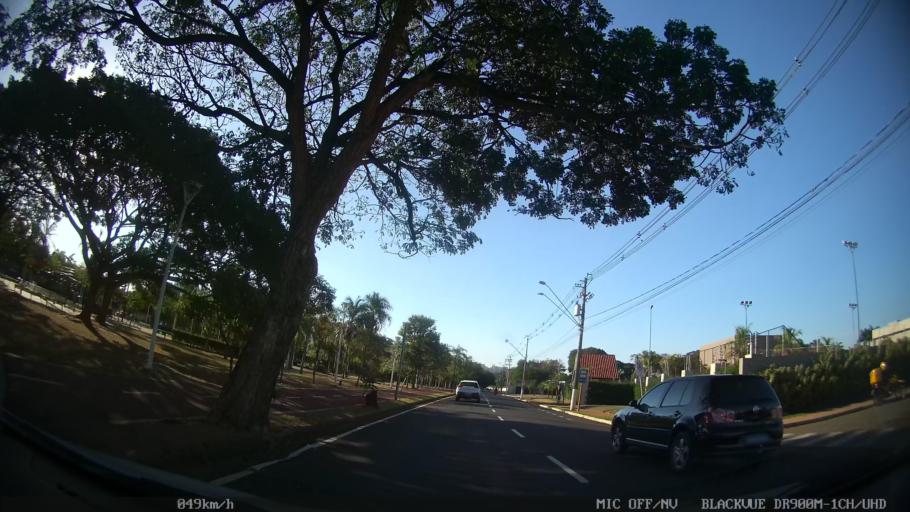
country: BR
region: Sao Paulo
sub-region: Sao Jose Do Rio Preto
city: Sao Jose do Rio Preto
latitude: -20.8491
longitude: -49.4123
